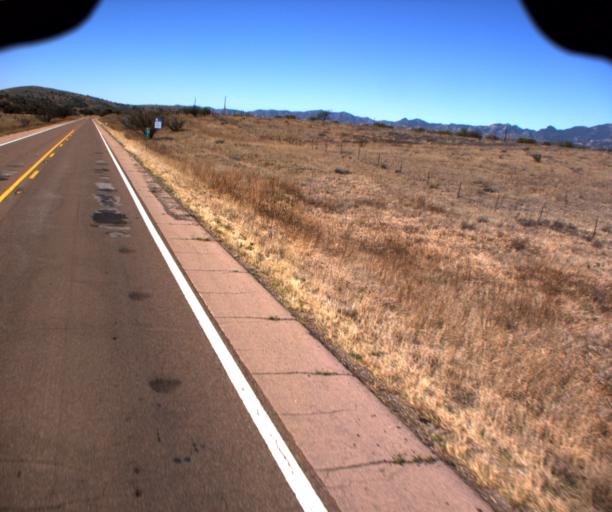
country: US
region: Arizona
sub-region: Pima County
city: Corona de Tucson
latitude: 31.6696
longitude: -110.6745
